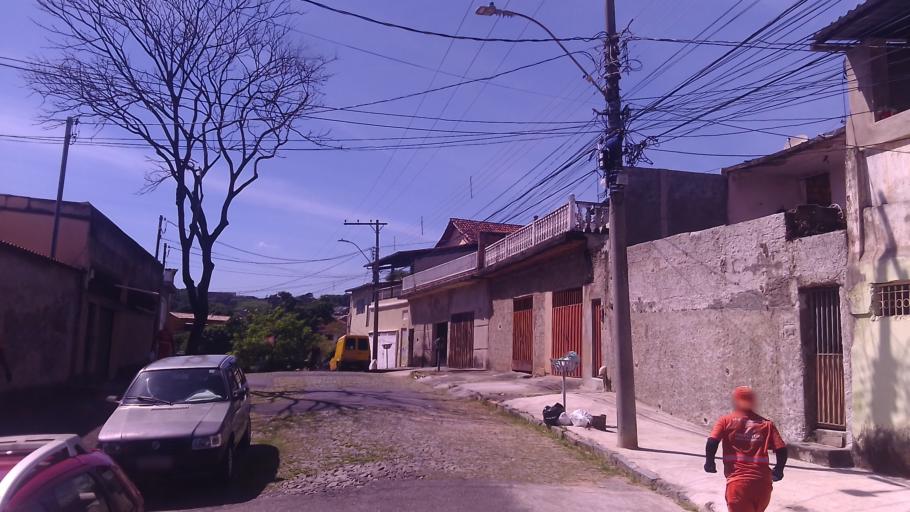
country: BR
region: Minas Gerais
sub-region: Contagem
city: Contagem
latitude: -19.9156
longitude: -44.0023
